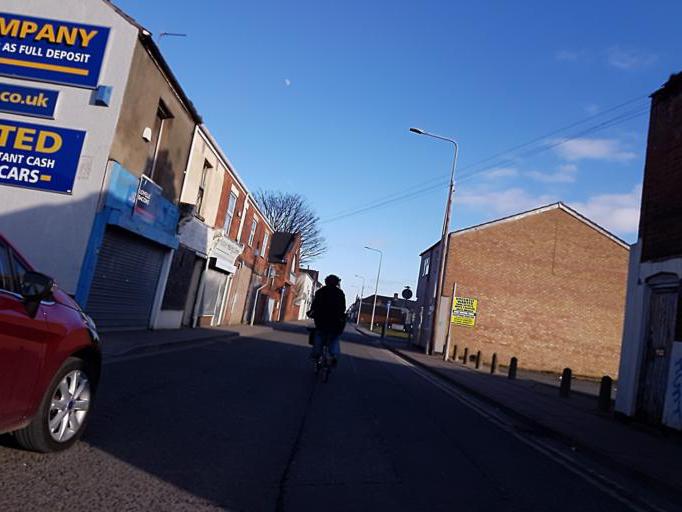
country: GB
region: England
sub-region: North East Lincolnshire
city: Grimsby
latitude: 53.5659
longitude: -0.0787
